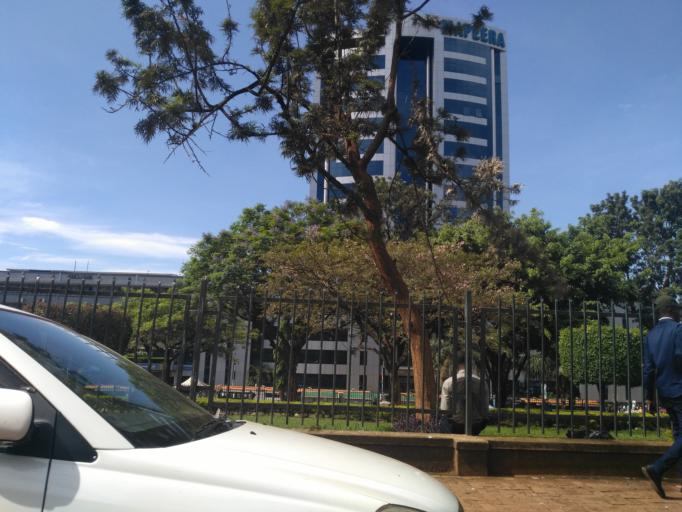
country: UG
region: Central Region
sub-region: Kampala District
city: Kampala
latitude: 0.3150
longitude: 32.5788
